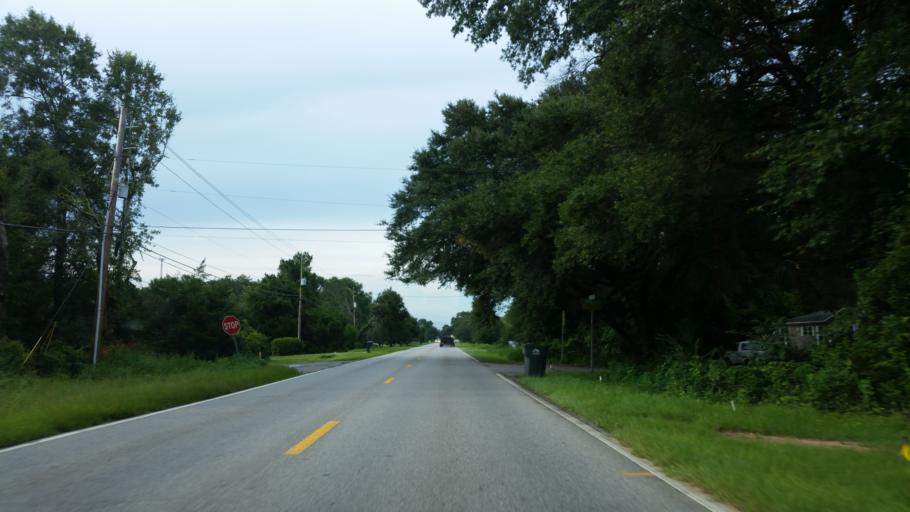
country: US
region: Florida
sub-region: Santa Rosa County
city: Pace
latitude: 30.5951
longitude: -87.1113
